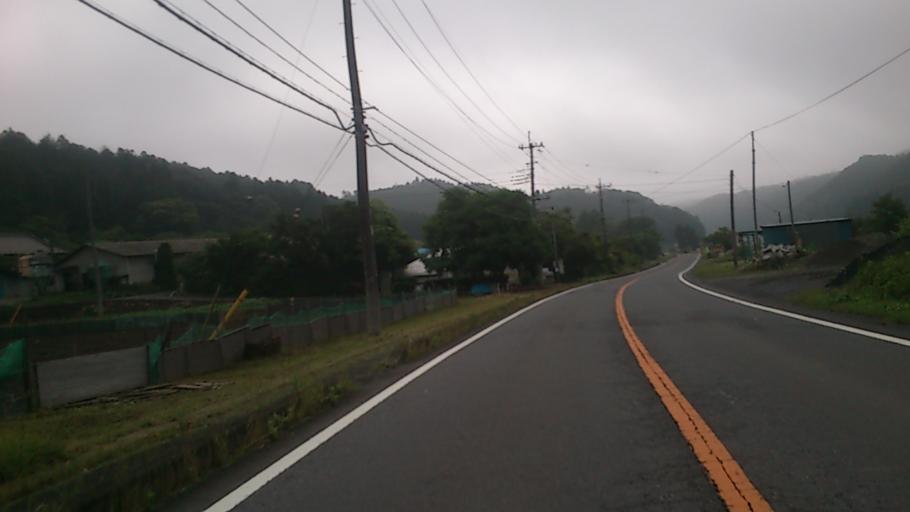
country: JP
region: Tochigi
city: Karasuyama
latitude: 36.6590
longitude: 140.2530
